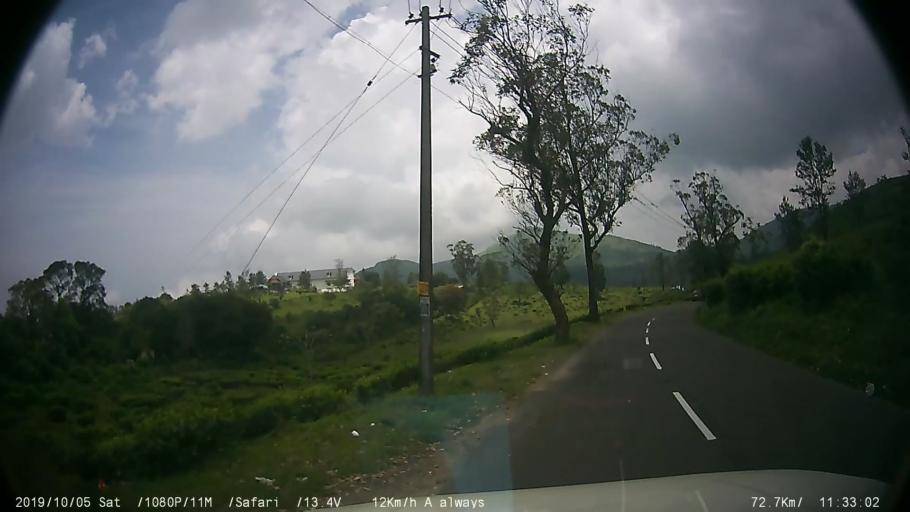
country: IN
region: Kerala
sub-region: Kottayam
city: Erattupetta
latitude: 9.5868
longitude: 76.9680
